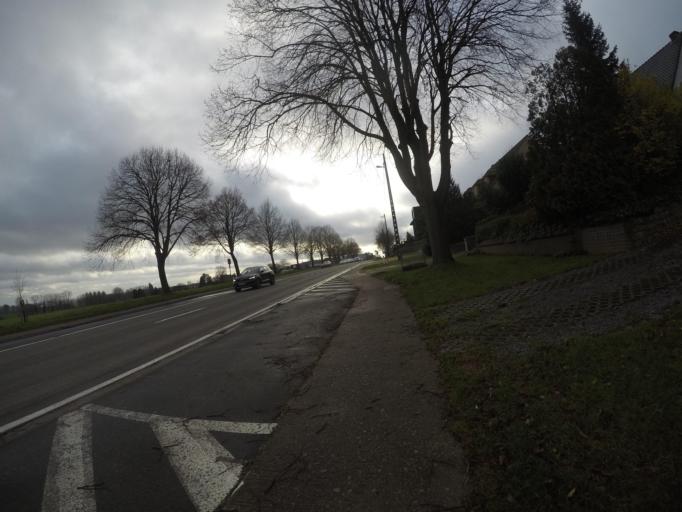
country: BE
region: Flanders
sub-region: Provincie Vlaams-Brabant
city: Gooik
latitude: 50.7988
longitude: 4.1282
